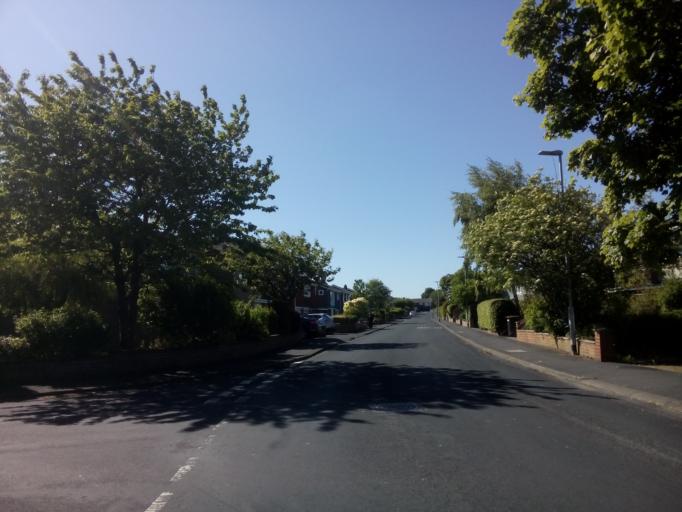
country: GB
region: England
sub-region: County Durham
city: Durham
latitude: 54.7862
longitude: -1.5464
